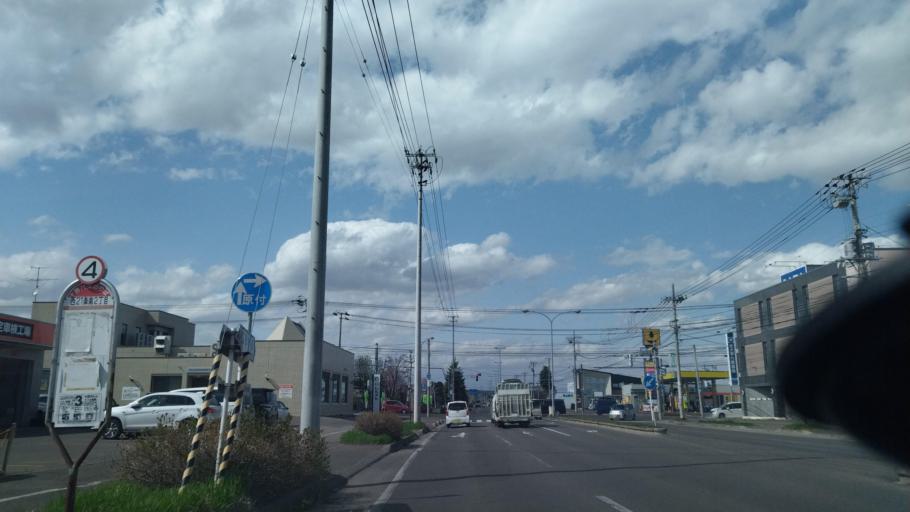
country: JP
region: Hokkaido
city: Obihiro
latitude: 42.9169
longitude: 143.1445
